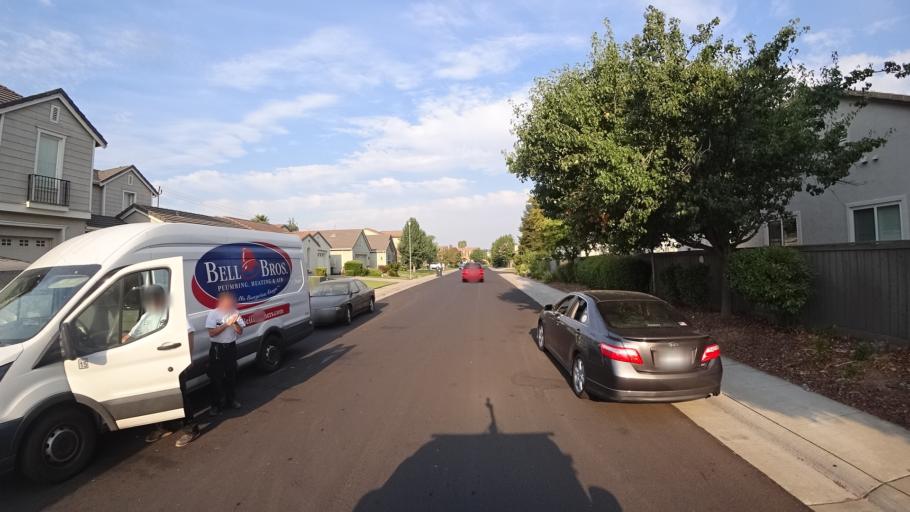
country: US
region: California
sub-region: Sacramento County
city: Laguna
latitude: 38.3800
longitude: -121.4222
